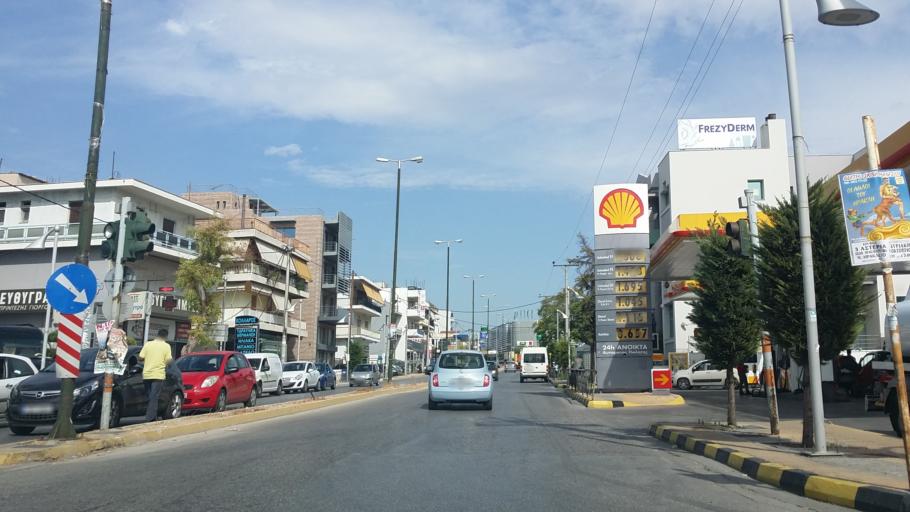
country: GR
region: Attica
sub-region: Nomarchia Athinas
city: Irakleio
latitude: 38.0508
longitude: 23.7498
